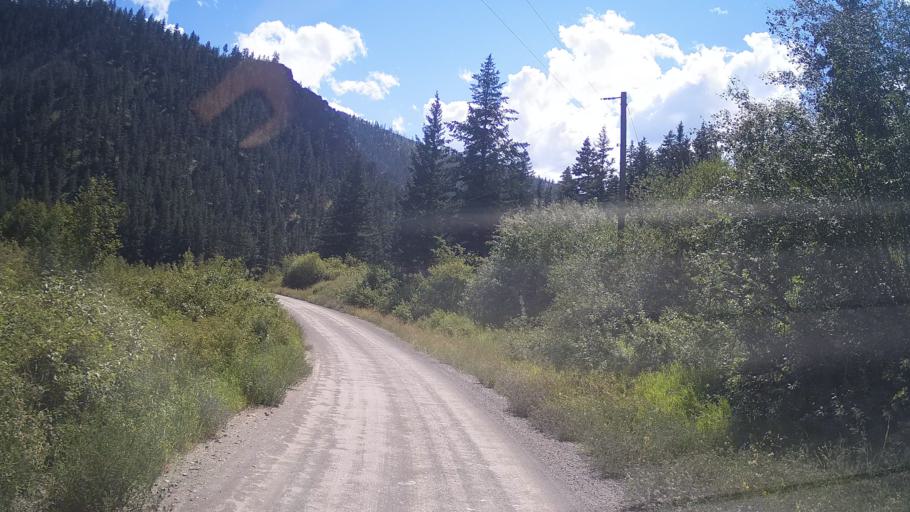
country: CA
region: British Columbia
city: Lillooet
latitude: 51.2348
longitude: -122.0517
